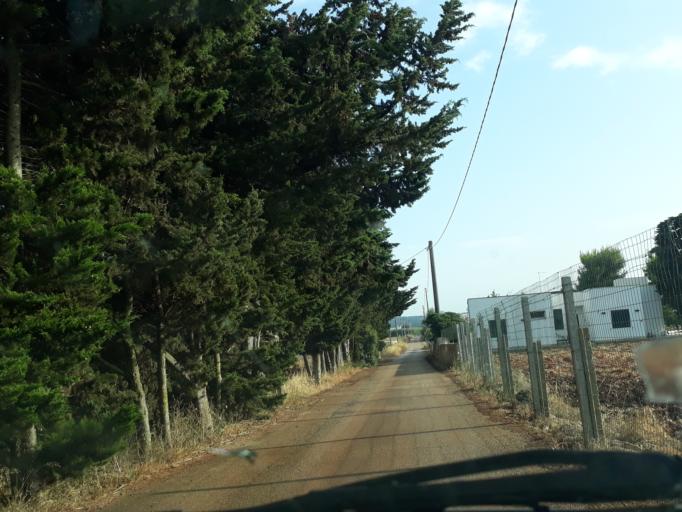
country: IT
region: Apulia
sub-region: Provincia di Brindisi
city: Carovigno
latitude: 40.7595
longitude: 17.6833
